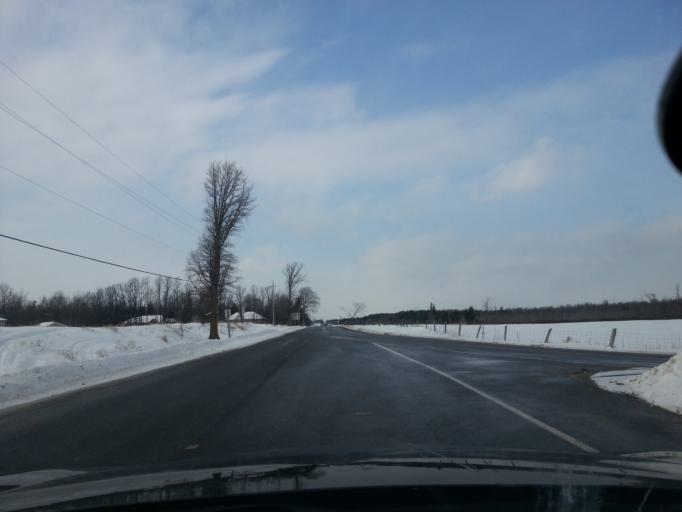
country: CA
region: Ontario
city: Carleton Place
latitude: 45.1594
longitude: -76.0358
